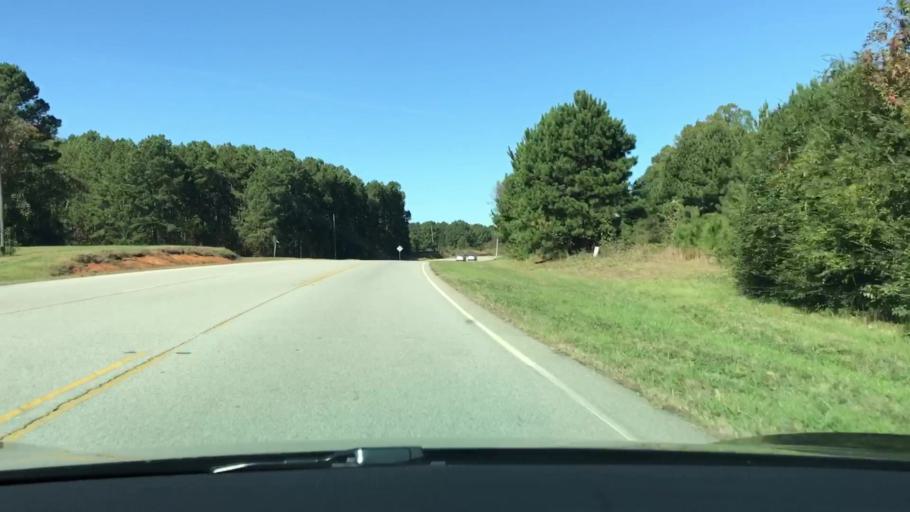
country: US
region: Georgia
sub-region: Warren County
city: Firing Range
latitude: 33.4848
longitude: -82.7928
